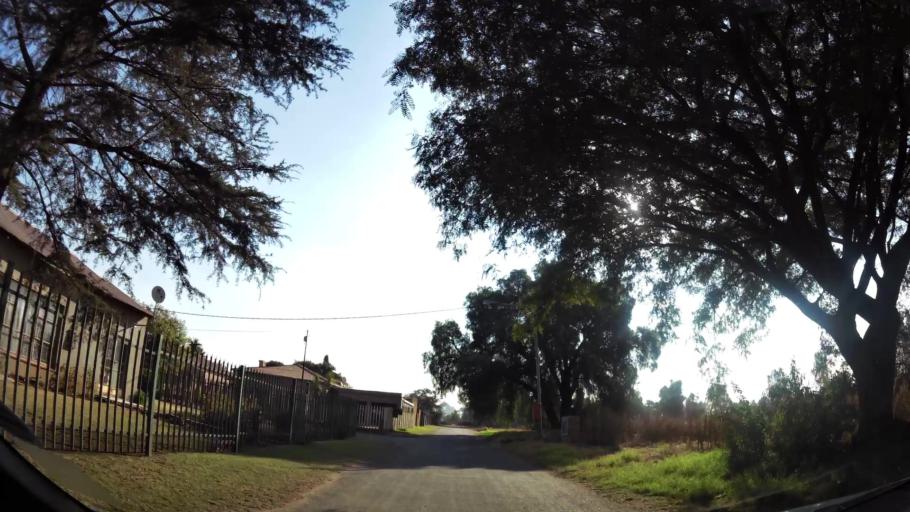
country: ZA
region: Gauteng
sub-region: Ekurhuleni Metropolitan Municipality
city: Brakpan
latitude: -26.2195
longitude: 28.3625
